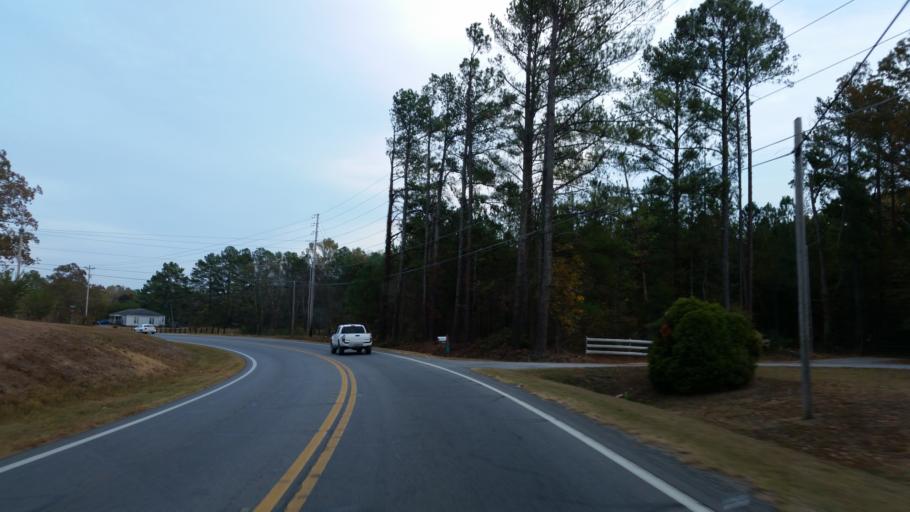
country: US
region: Georgia
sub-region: Gordon County
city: Calhoun
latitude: 34.5950
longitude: -84.9094
